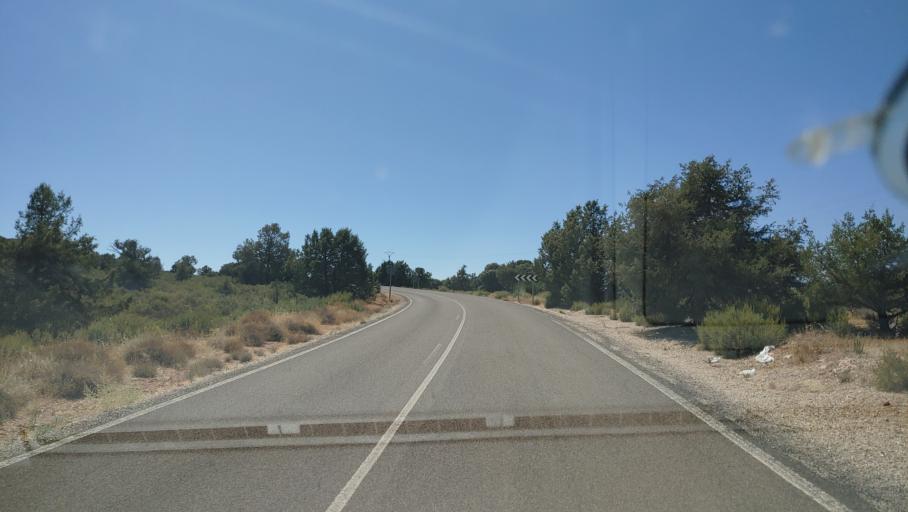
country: ES
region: Castille-La Mancha
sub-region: Provincia de Ciudad Real
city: Villahermosa
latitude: 38.8516
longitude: -2.8060
